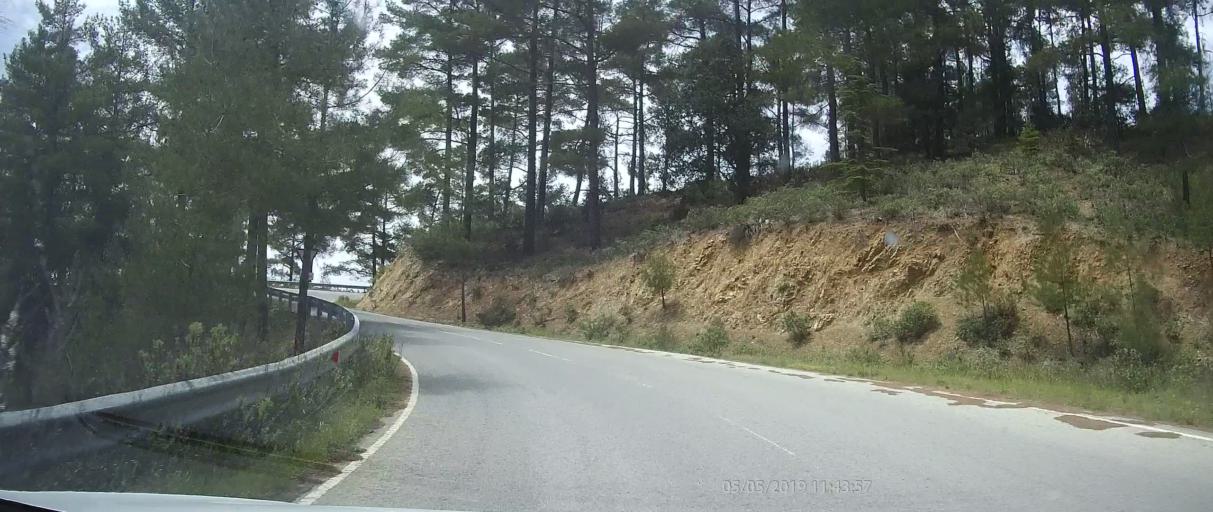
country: CY
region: Lefkosia
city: Kato Pyrgos
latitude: 35.0106
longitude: 32.6687
